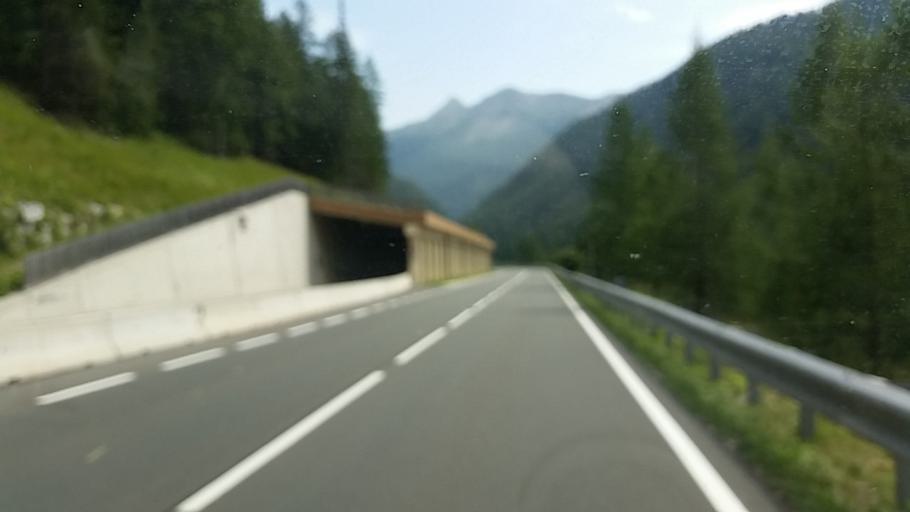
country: AT
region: Salzburg
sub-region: Politischer Bezirk Tamsweg
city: Tweng
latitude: 47.2278
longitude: 13.5798
